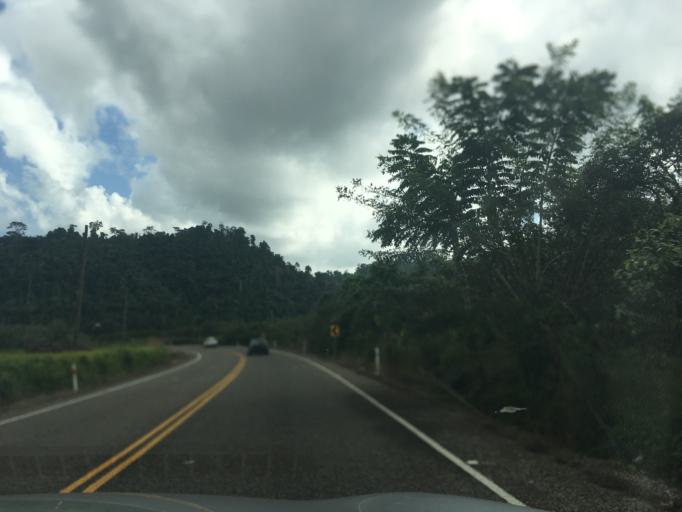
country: BZ
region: Cayo
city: Belmopan
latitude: 17.1467
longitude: -88.6984
